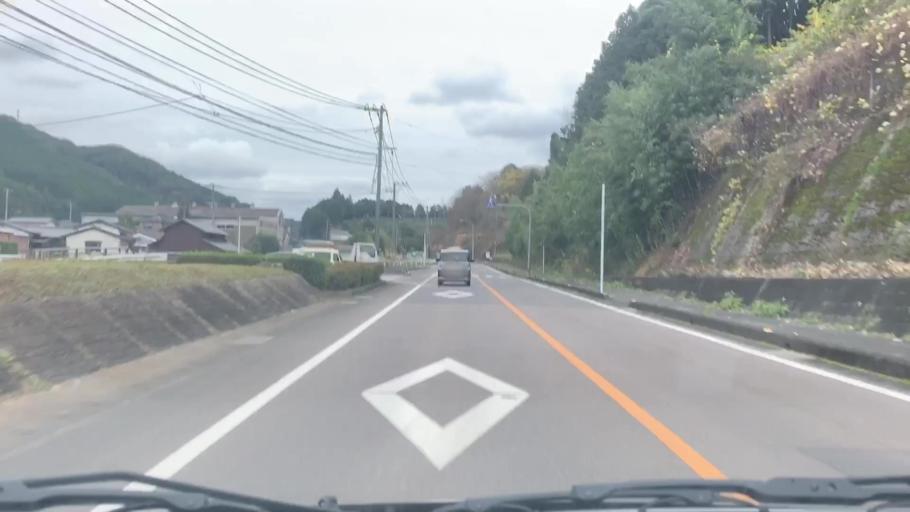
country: JP
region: Saga Prefecture
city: Ureshinomachi-shimojuku
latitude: 33.0987
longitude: 130.0011
